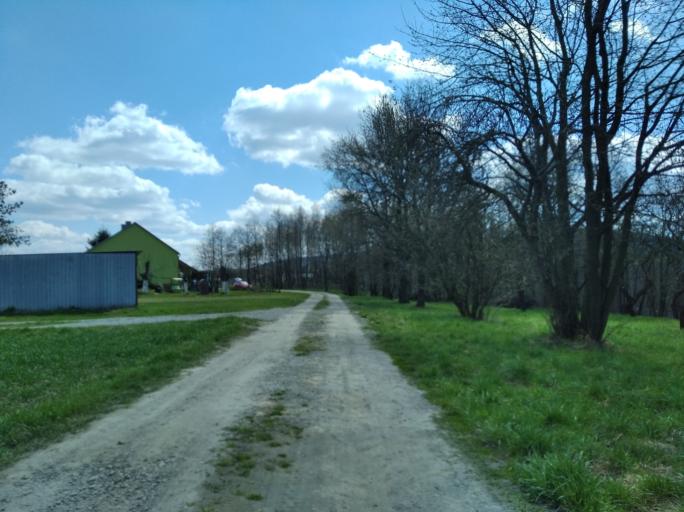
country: PL
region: Subcarpathian Voivodeship
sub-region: Powiat strzyzowski
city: Wysoka Strzyzowska
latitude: 49.8467
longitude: 21.7675
